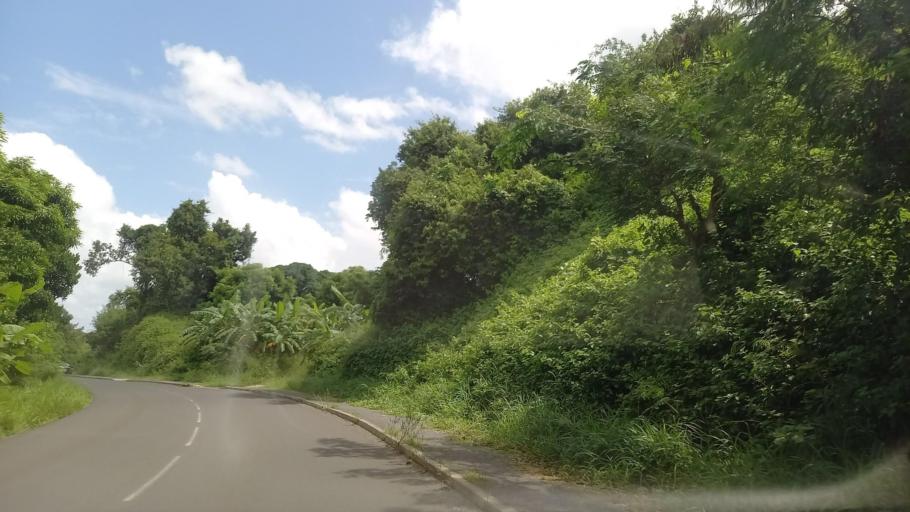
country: YT
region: Boueni
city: Boueni
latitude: -12.9239
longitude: 45.0952
